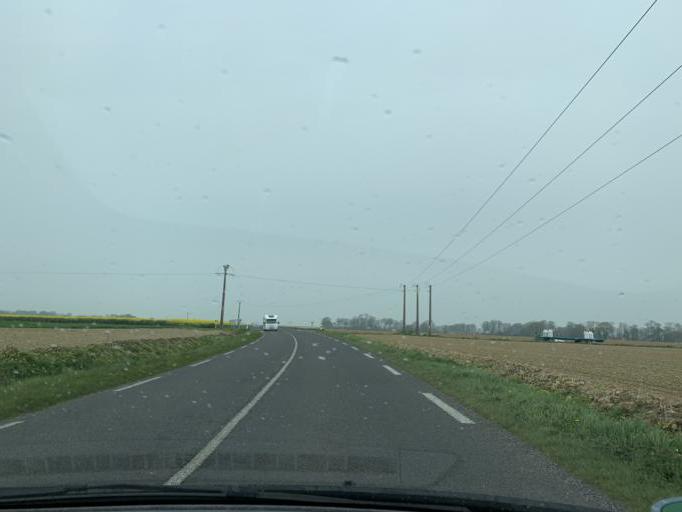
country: FR
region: Haute-Normandie
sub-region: Departement de la Seine-Maritime
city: Cany-Barville
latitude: 49.7941
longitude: 0.6623
